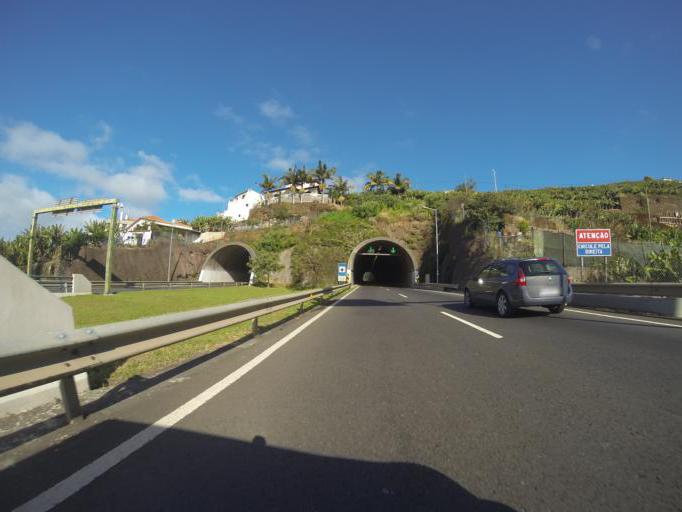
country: PT
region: Madeira
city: Camara de Lobos
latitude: 32.6604
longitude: -16.9767
